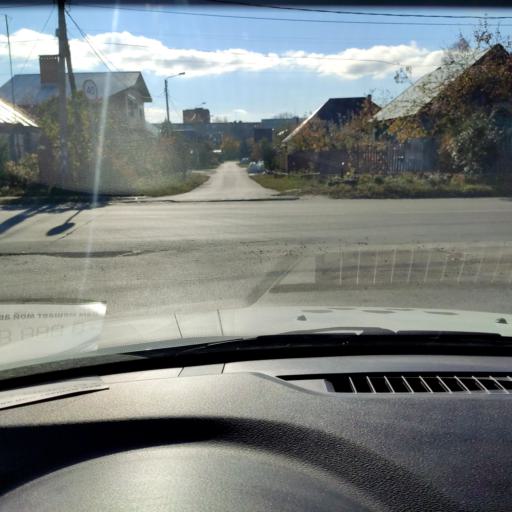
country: RU
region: Samara
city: Tol'yatti
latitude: 53.5320
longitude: 49.4008
